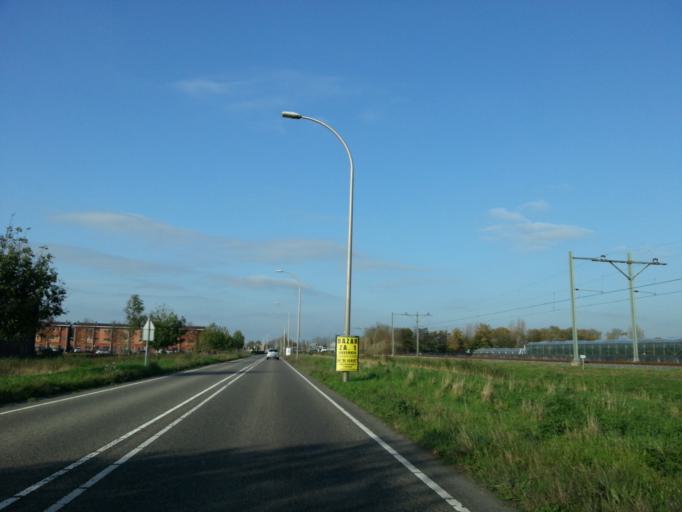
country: NL
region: South Holland
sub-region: Gemeente Pijnacker-Nootdorp
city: Pijnacker
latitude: 52.0445
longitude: 4.4163
